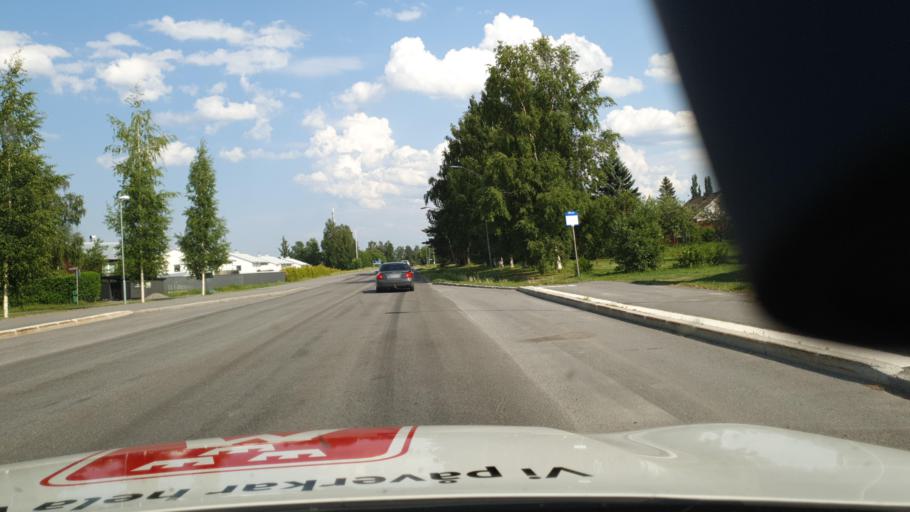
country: SE
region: Vaesterbotten
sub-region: Skelleftea Kommun
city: Viken
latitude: 64.7470
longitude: 20.9143
